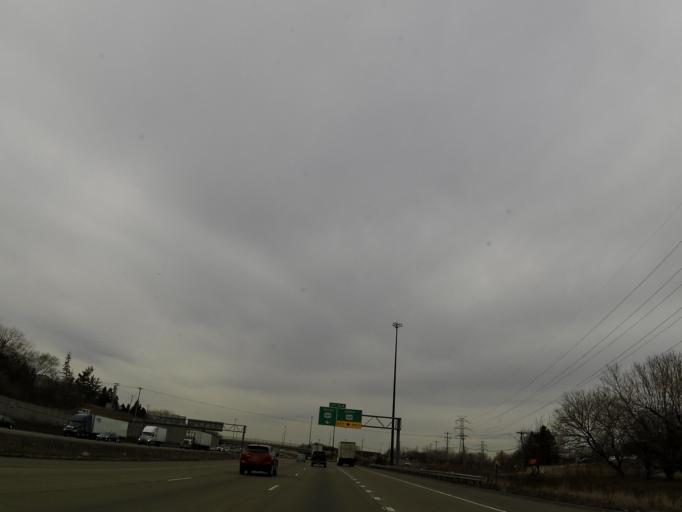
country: US
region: Minnesota
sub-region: Hennepin County
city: Edina
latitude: 44.8605
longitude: -93.3779
